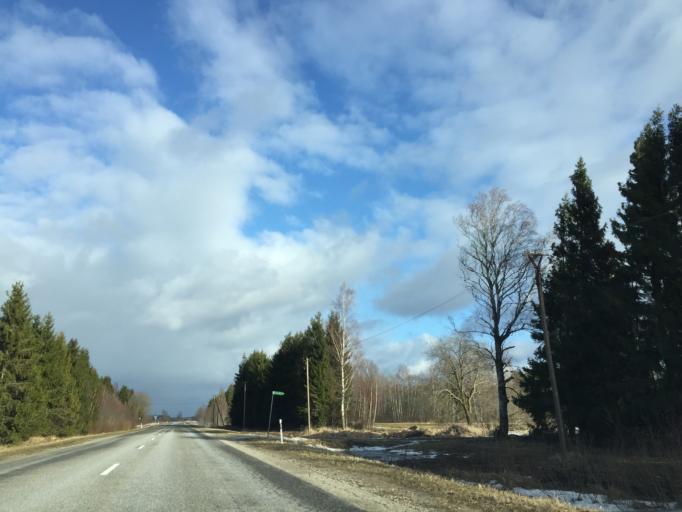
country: LV
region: Aloja
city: Staicele
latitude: 57.8702
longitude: 24.5702
